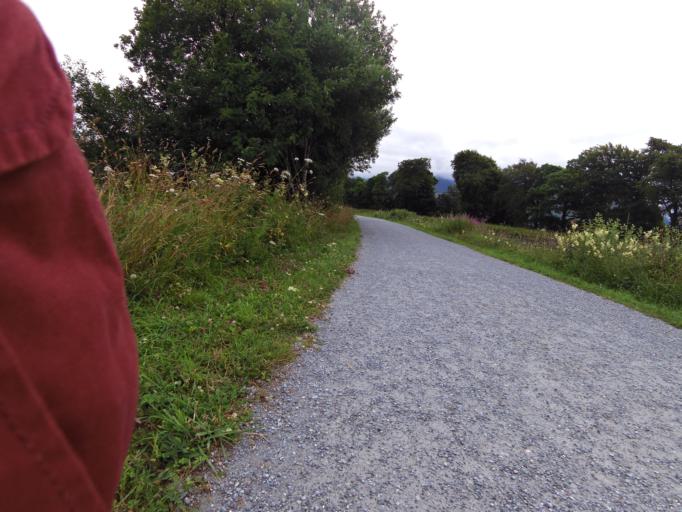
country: GB
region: Scotland
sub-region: Highland
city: Fort William
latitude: 56.8408
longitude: -5.1102
